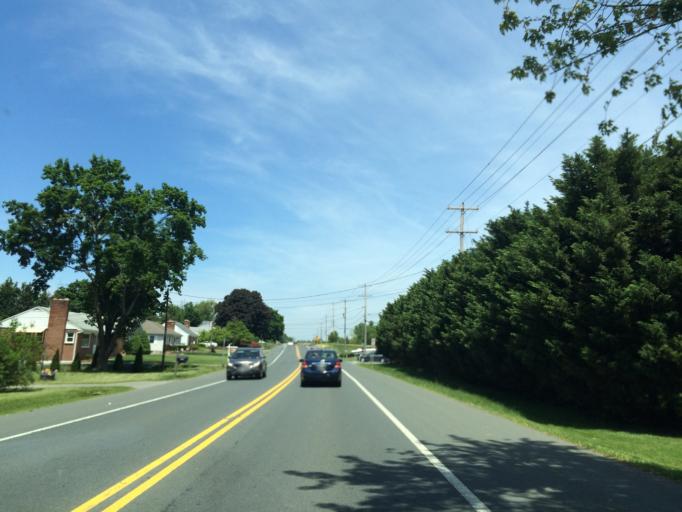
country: US
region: Maryland
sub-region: Washington County
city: Saint James
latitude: 39.5850
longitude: -77.7298
